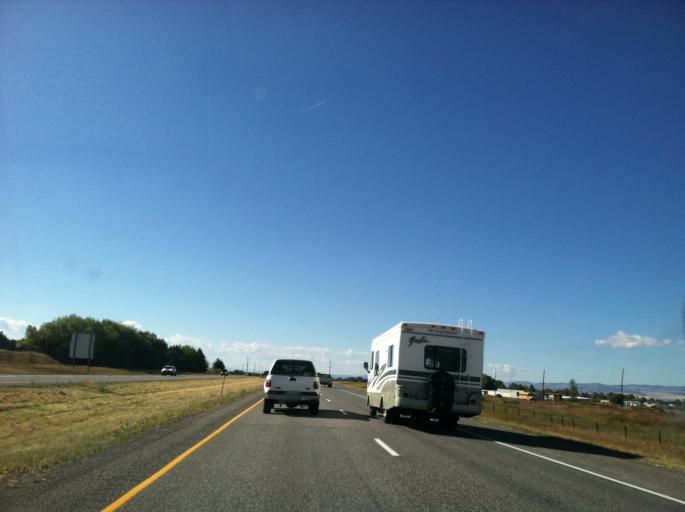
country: US
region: Montana
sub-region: Gallatin County
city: Bozeman
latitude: 45.7336
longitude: -111.0974
